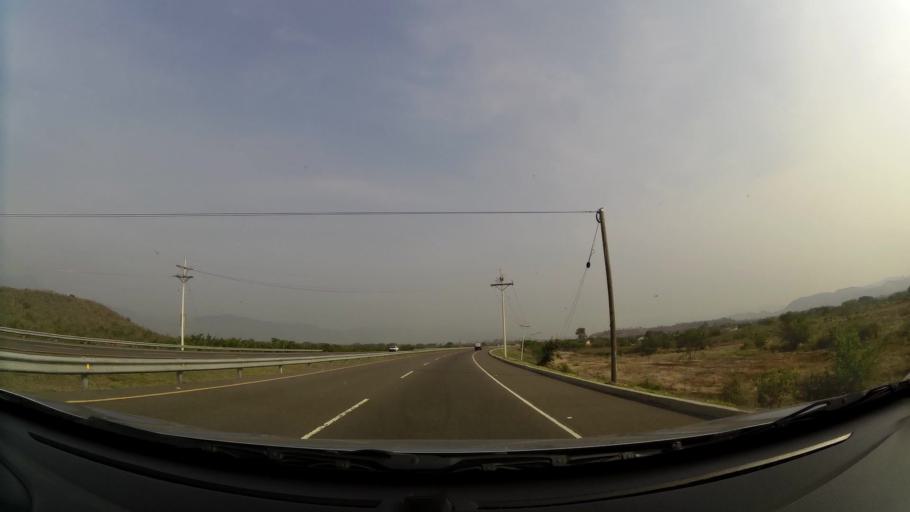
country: HN
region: Comayagua
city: Comayagua
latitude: 14.4377
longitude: -87.6574
